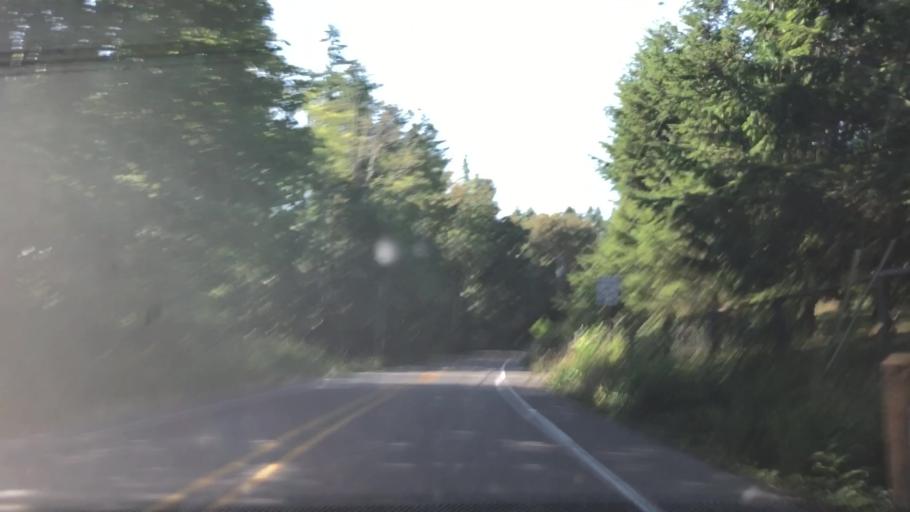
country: US
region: Washington
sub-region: Kitsap County
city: Kingston
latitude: 47.7803
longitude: -122.4999
